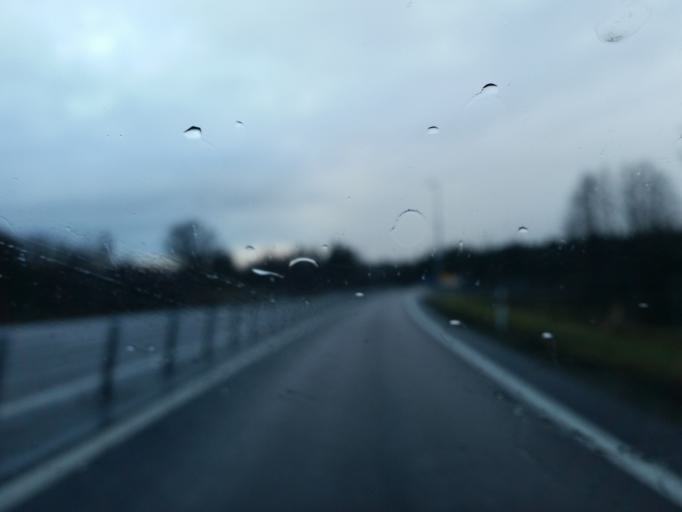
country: SE
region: Vaestra Goetaland
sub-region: Boras Kommun
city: Ganghester
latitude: 57.6774
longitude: 12.9751
